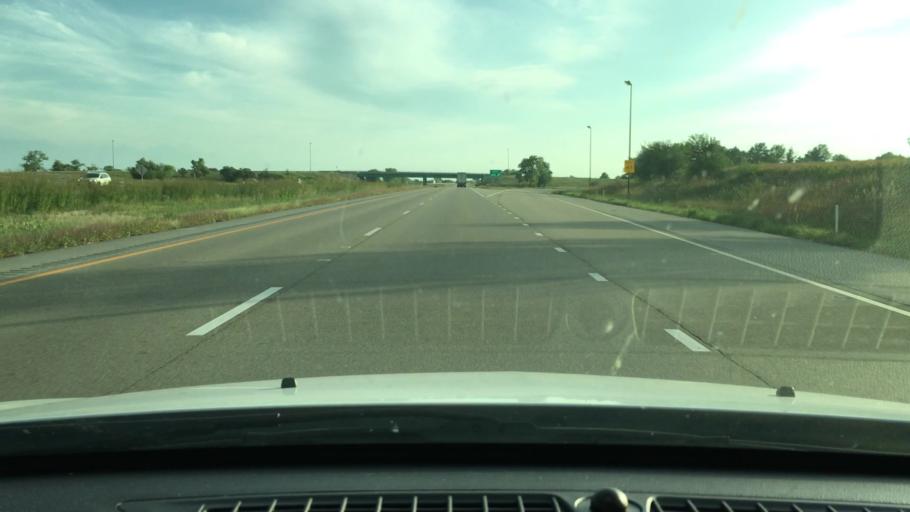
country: US
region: Illinois
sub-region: Logan County
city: Atlanta
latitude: 40.2630
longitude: -89.2168
